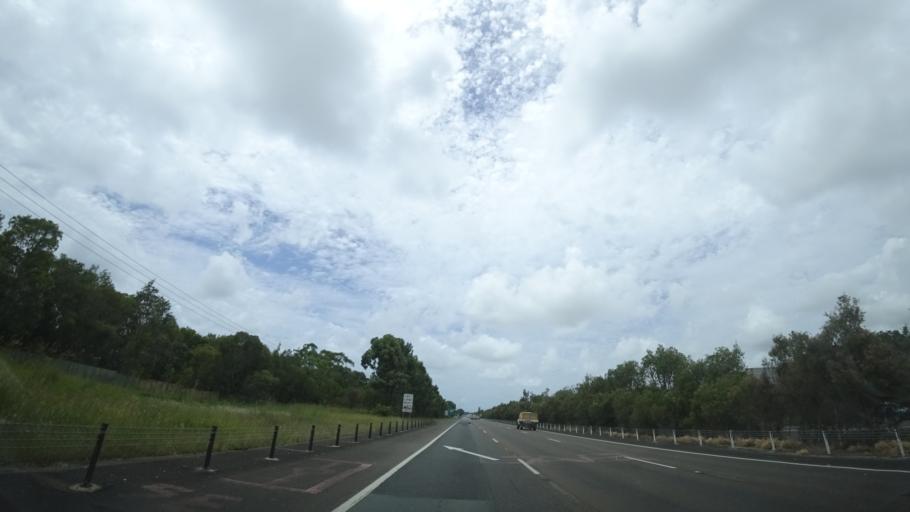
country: AU
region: Queensland
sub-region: Sunshine Coast
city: Mooloolaba
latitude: -26.6845
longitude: 153.1045
